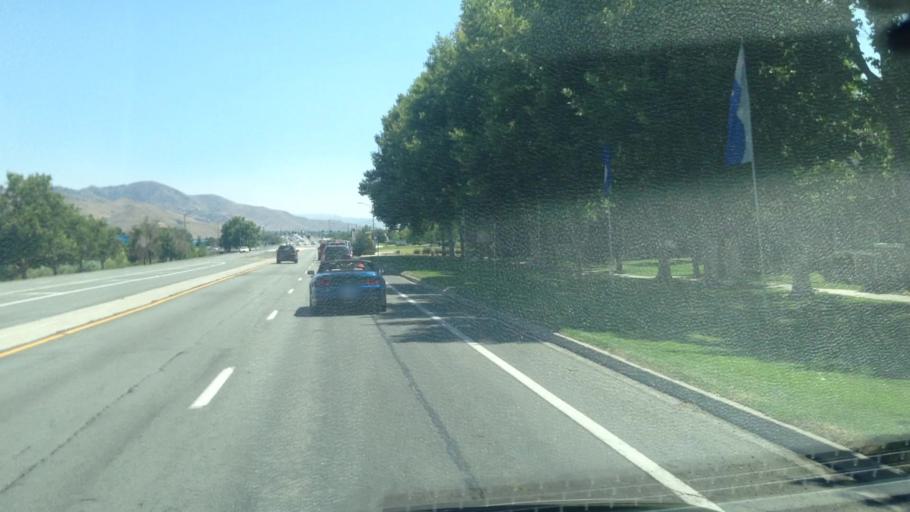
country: US
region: Nevada
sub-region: Washoe County
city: Sparks
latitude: 39.5377
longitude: -119.7155
